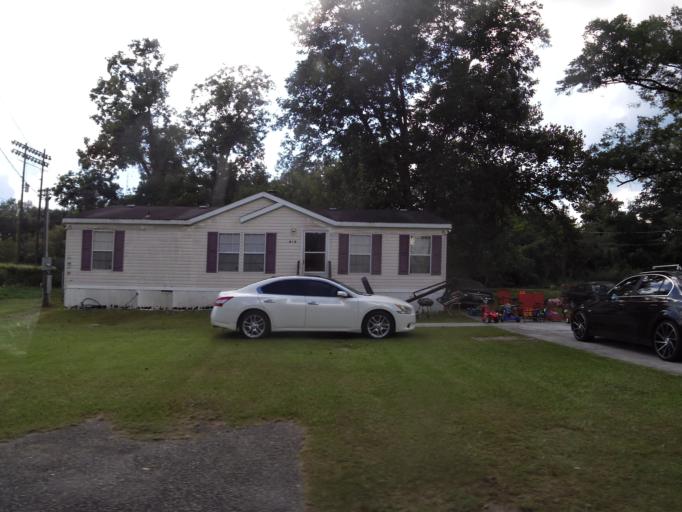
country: US
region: Georgia
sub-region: Lowndes County
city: Valdosta
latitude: 30.8256
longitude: -83.2803
